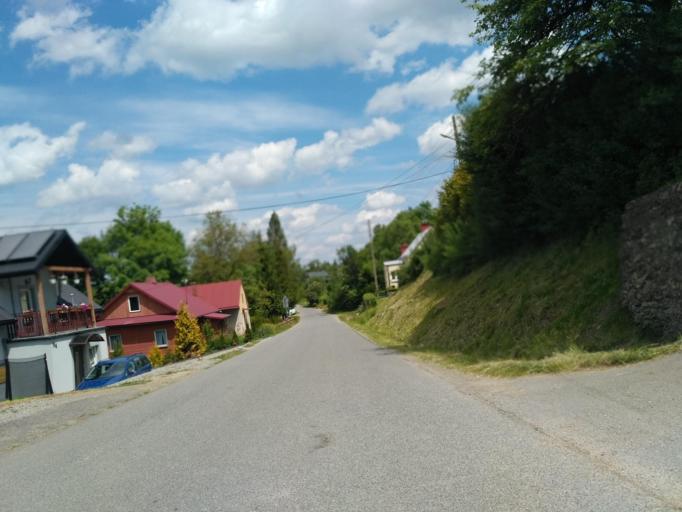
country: PL
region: Subcarpathian Voivodeship
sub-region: Powiat krosnienski
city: Dukla
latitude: 49.5678
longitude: 21.6144
